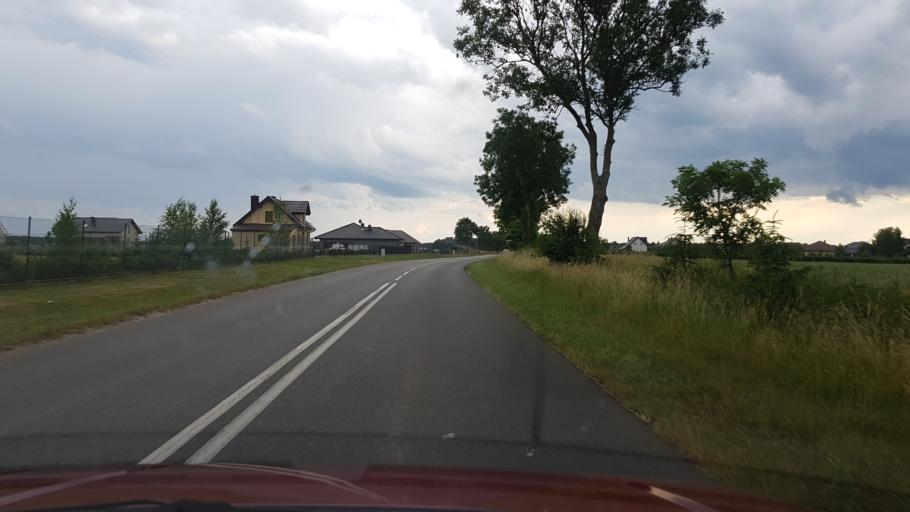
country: PL
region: West Pomeranian Voivodeship
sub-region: Powiat gryficki
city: Gryfice
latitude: 53.8940
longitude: 15.1754
